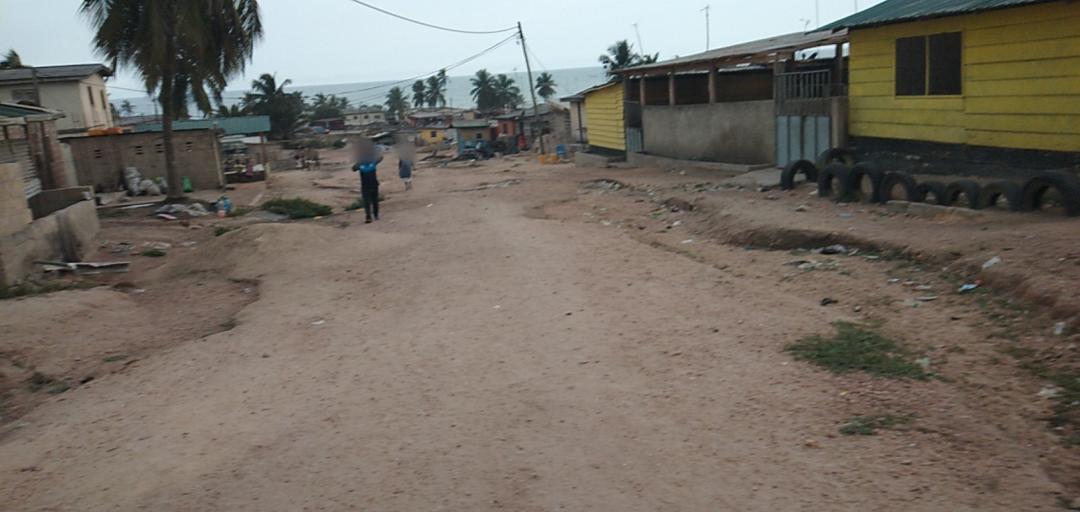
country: GH
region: Central
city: Winneba
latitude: 5.3513
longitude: -0.6140
